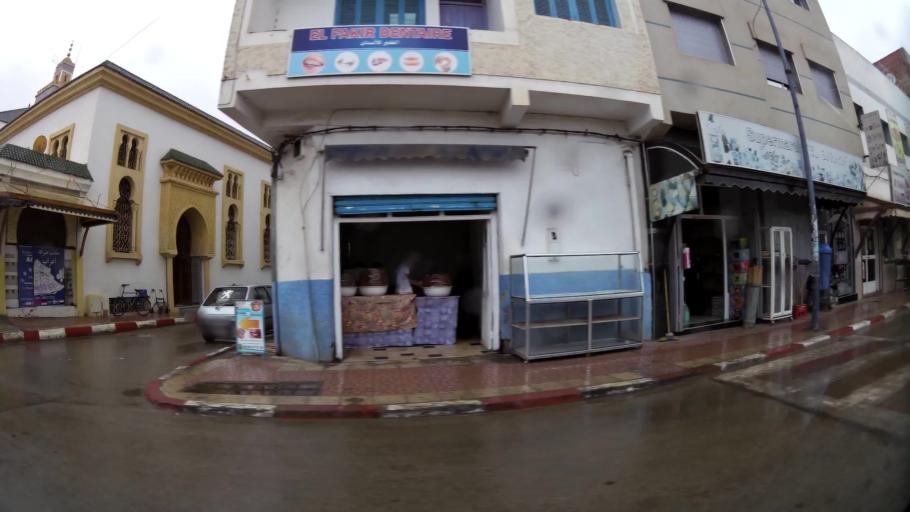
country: MA
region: Taza-Al Hoceima-Taounate
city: Imzourene
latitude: 35.1498
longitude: -3.8489
